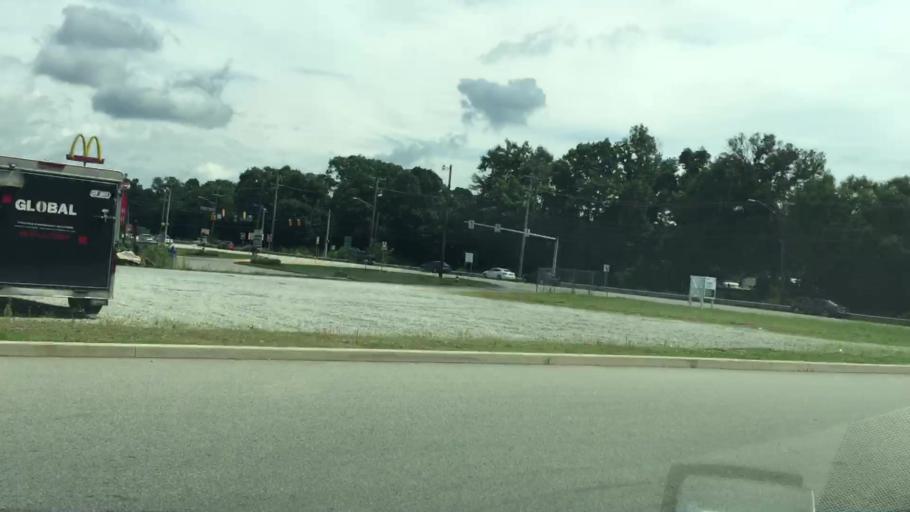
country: US
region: Pennsylvania
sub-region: Allegheny County
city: Oakmont
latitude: 40.5388
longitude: -79.8326
